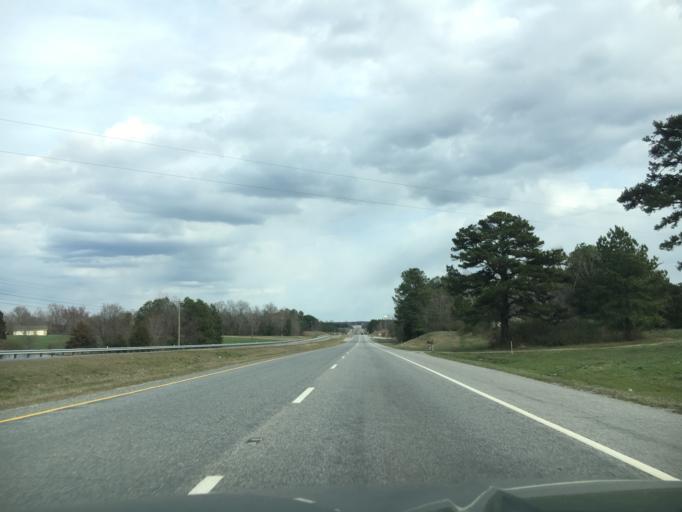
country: US
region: Virginia
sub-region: Mecklenburg County
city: Boydton
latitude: 36.6714
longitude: -78.2573
